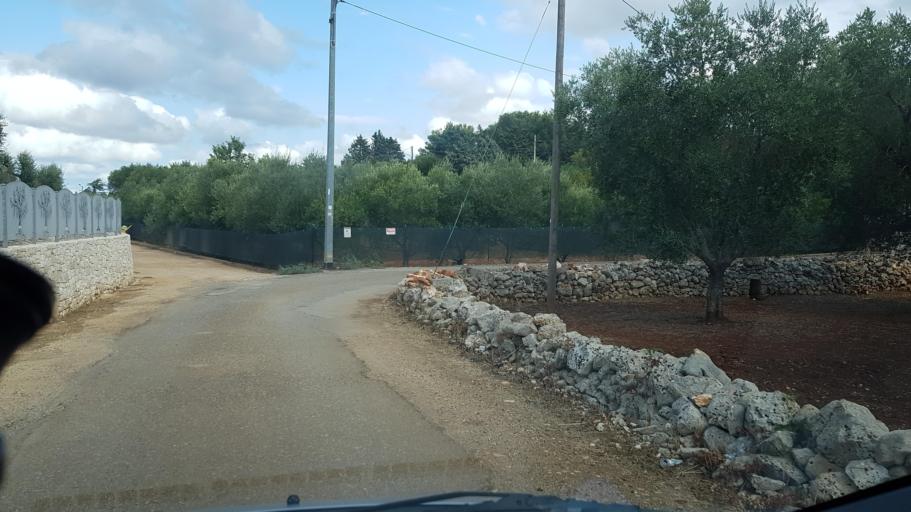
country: IT
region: Apulia
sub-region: Provincia di Brindisi
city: San Vito dei Normanni
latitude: 40.6675
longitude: 17.7193
